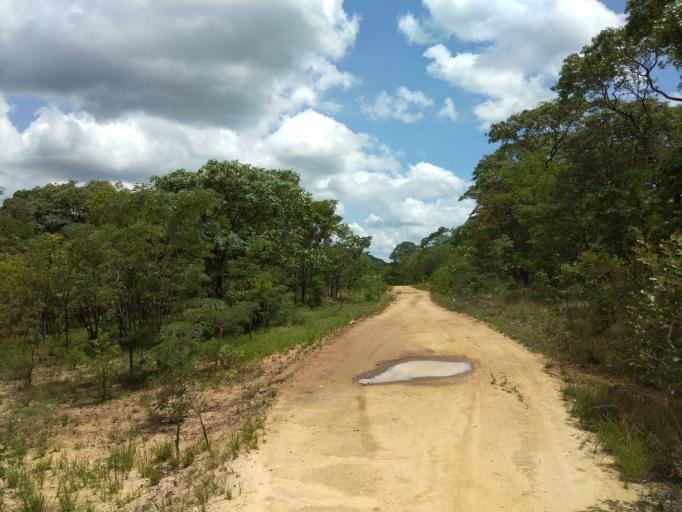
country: ZM
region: Central
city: Mkushi
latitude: -14.0197
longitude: 29.9610
